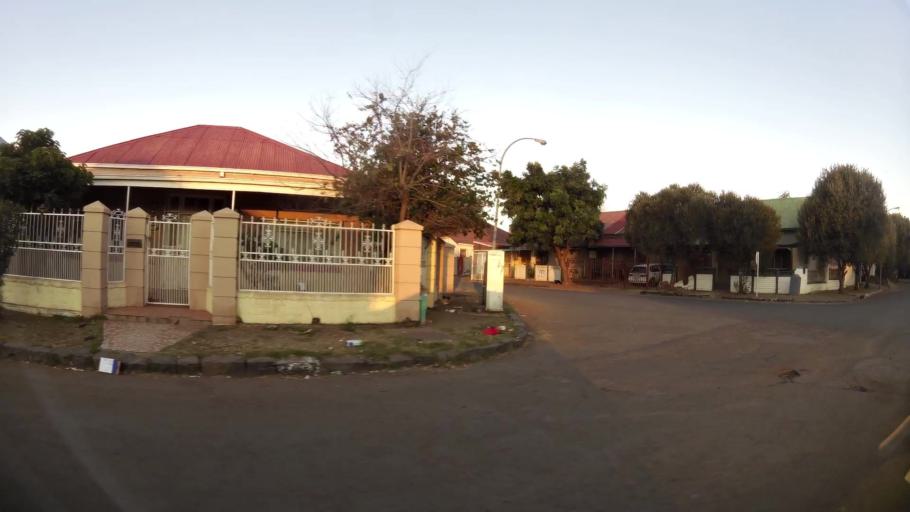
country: ZA
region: Northern Cape
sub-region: Frances Baard District Municipality
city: Kimberley
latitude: -28.7348
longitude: 24.7670
